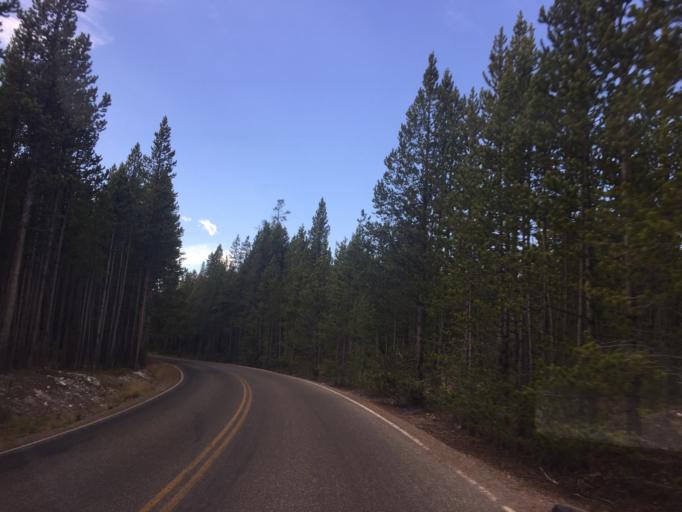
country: US
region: Montana
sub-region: Gallatin County
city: West Yellowstone
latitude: 44.7300
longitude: -110.4737
